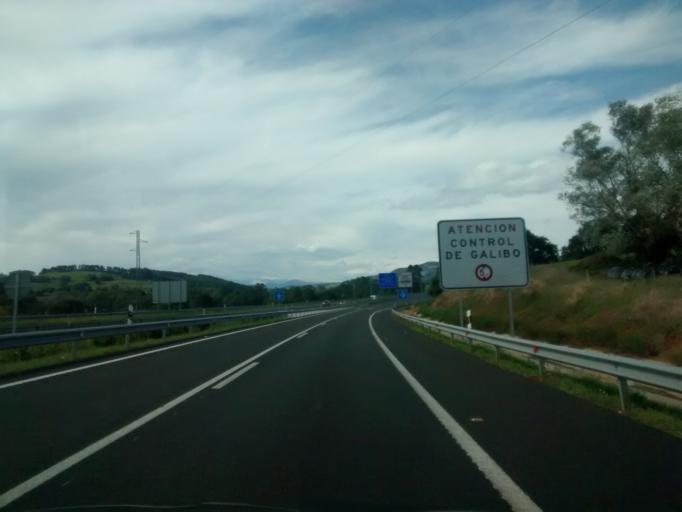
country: ES
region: Cantabria
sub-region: Provincia de Cantabria
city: El Astillero
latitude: 43.3849
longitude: -3.8469
